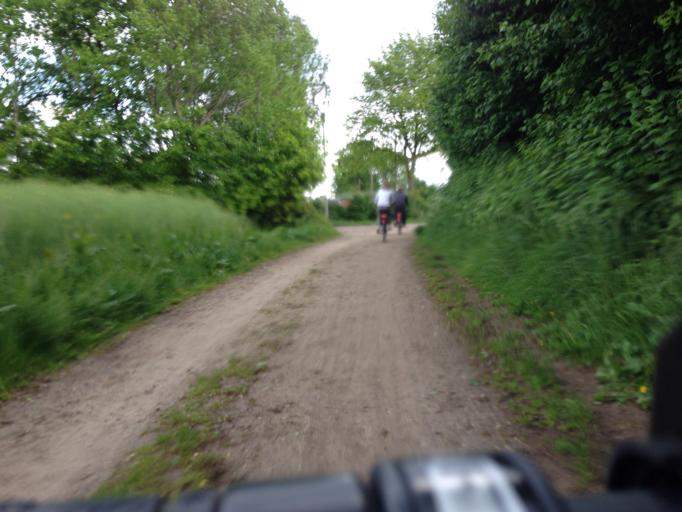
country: DE
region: Schleswig-Holstein
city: Barsbuettel
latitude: 53.5839
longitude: 10.1869
